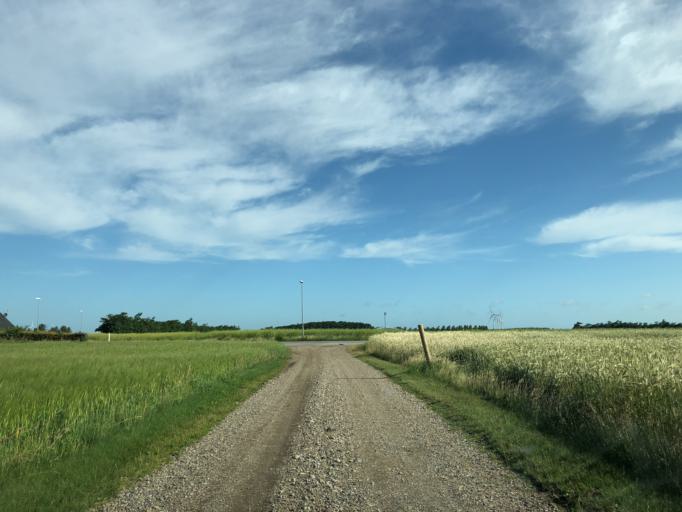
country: DK
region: Central Jutland
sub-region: Holstebro Kommune
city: Ulfborg
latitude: 56.3385
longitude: 8.3080
